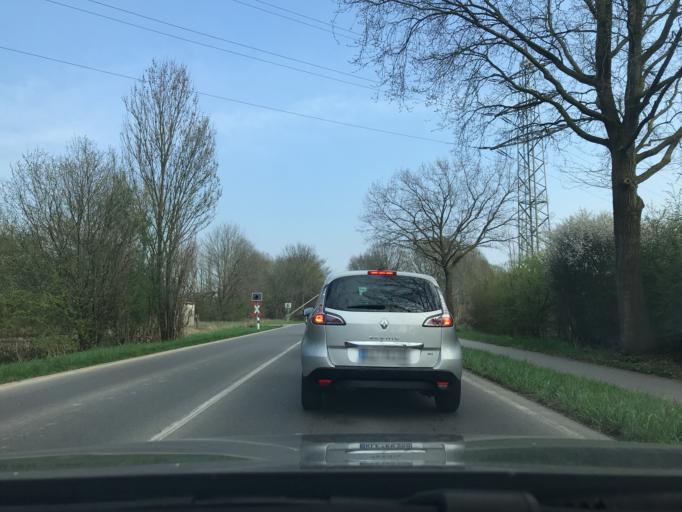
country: DE
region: North Rhine-Westphalia
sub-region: Regierungsbezirk Dusseldorf
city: Kleve
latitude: 51.7802
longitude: 6.1598
